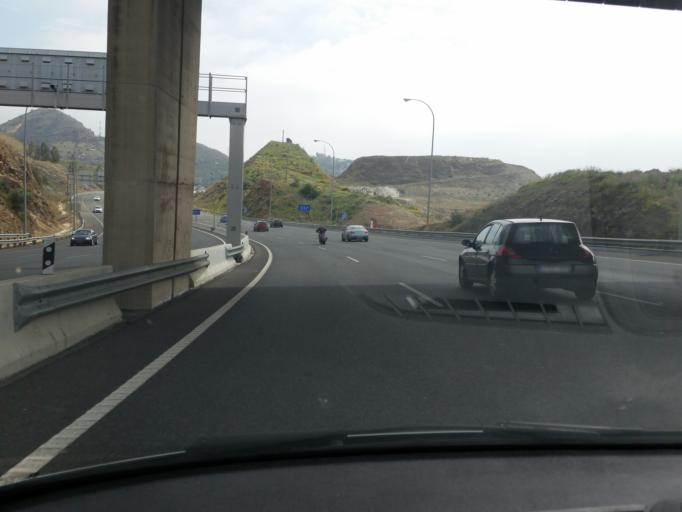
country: ES
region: Andalusia
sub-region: Provincia de Malaga
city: Malaga
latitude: 36.7403
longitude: -4.4006
